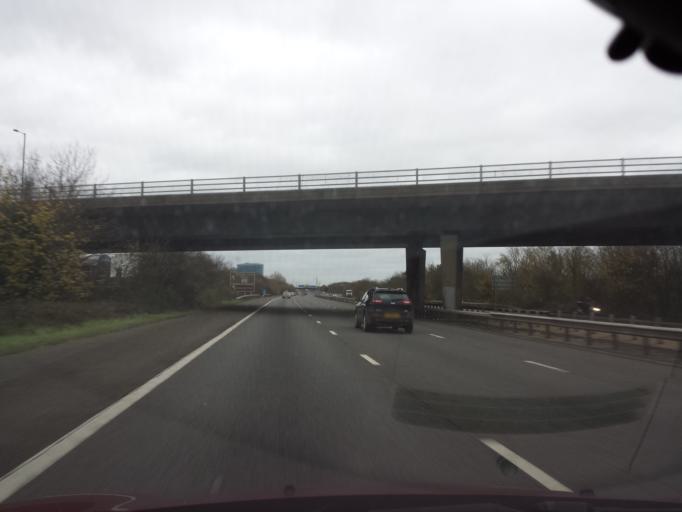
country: GB
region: England
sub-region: Surrey
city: Sunbury-on-Thames
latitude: 51.4138
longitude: -0.4311
